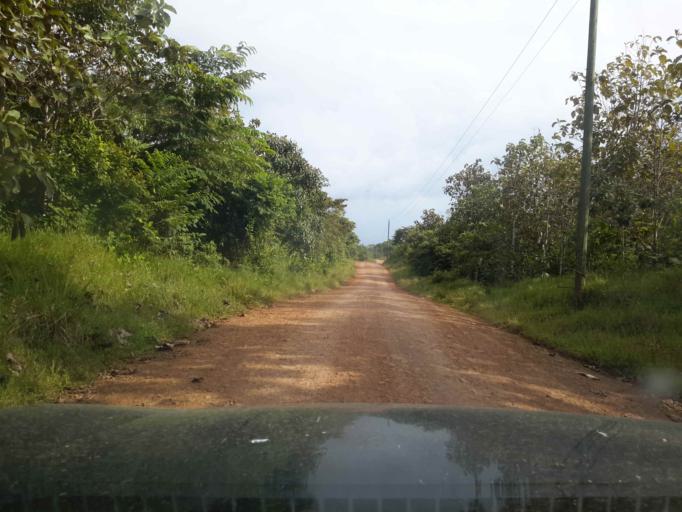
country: CR
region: Alajuela
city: Los Chiles
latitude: 11.0862
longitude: -84.5409
